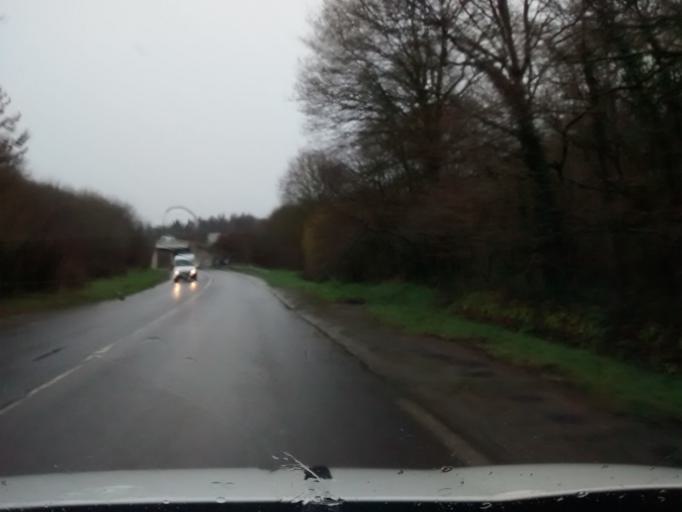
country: FR
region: Brittany
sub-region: Departement d'Ille-et-Vilaine
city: Gosne
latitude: 48.2391
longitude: -1.4626
